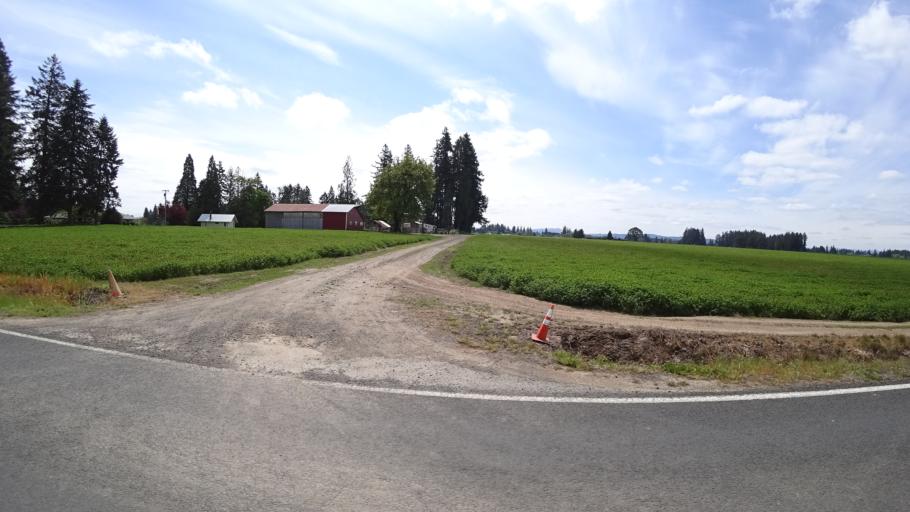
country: US
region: Oregon
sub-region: Washington County
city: Hillsboro
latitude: 45.5439
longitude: -123.0075
